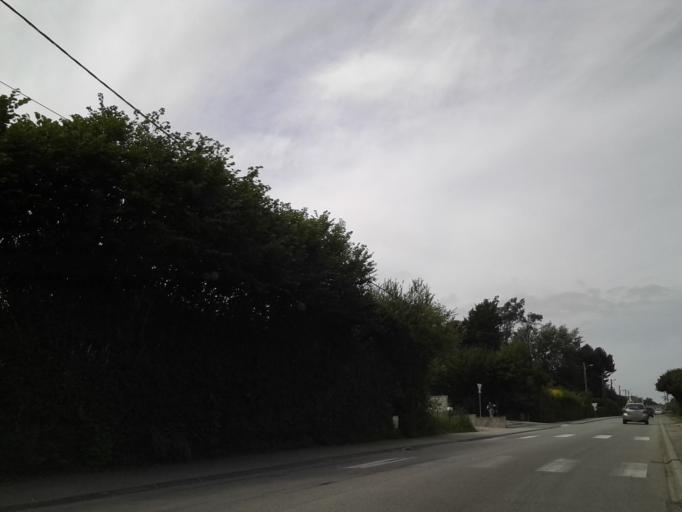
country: FR
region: Lower Normandy
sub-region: Departement de la Manche
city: Bricquebec
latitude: 49.4653
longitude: -1.6385
